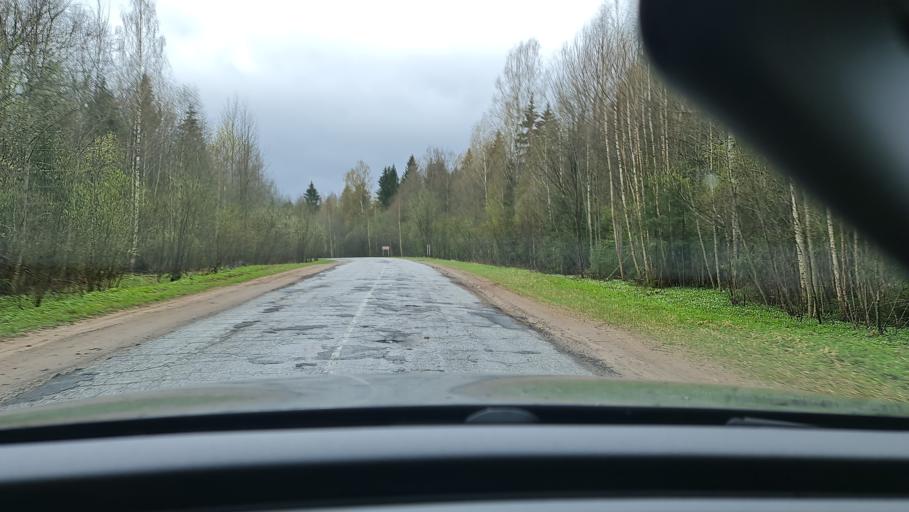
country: RU
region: Novgorod
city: Marevo
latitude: 57.2934
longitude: 32.0816
